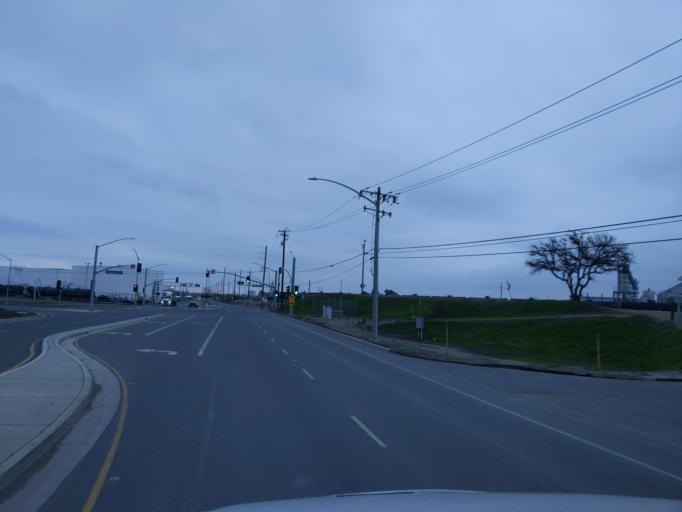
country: US
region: California
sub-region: San Joaquin County
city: Country Club
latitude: 37.9450
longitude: -121.3376
